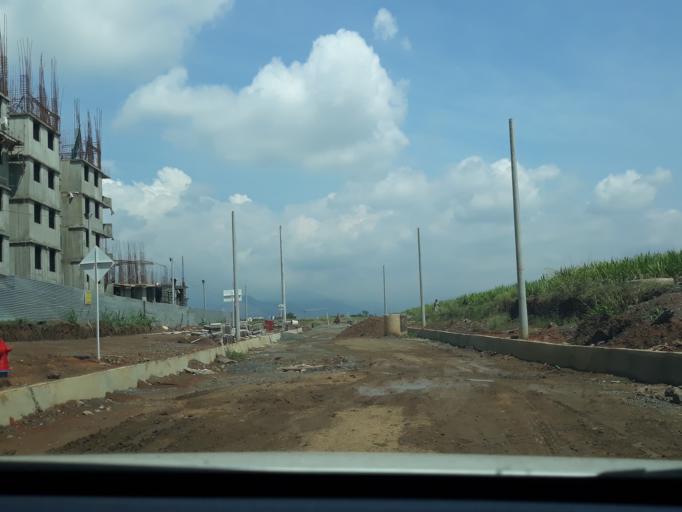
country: CO
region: Valle del Cauca
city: Cali
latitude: 3.3724
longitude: -76.5047
